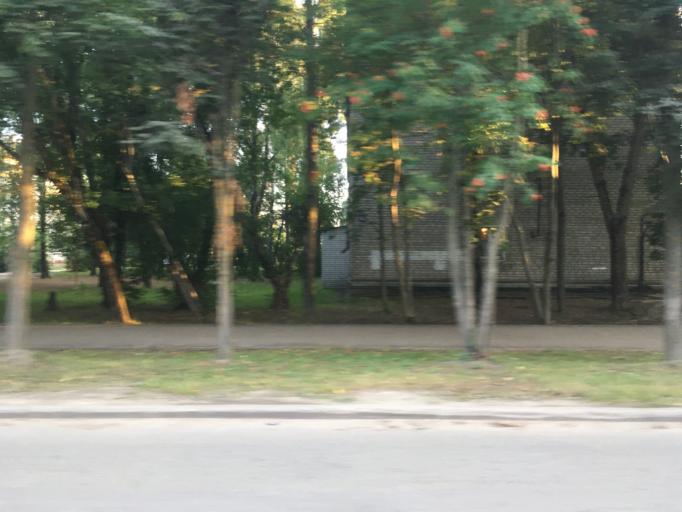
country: RU
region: Mariy-El
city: Yoshkar-Ola
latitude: 56.6480
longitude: 47.8804
